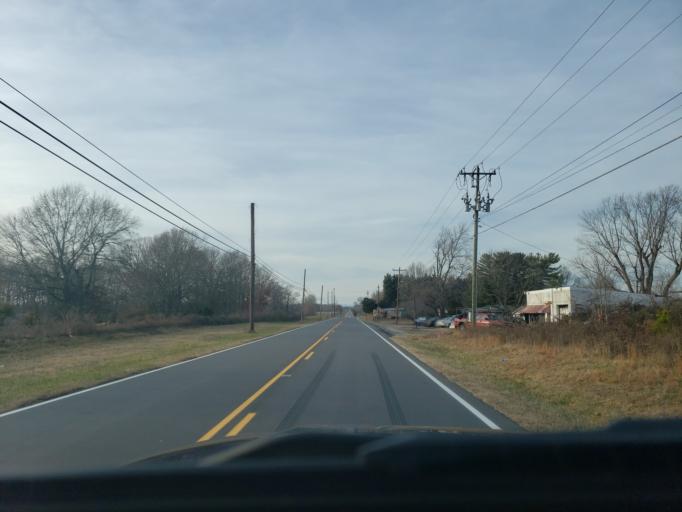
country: US
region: North Carolina
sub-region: Cleveland County
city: Boiling Springs
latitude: 35.3092
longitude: -81.7326
